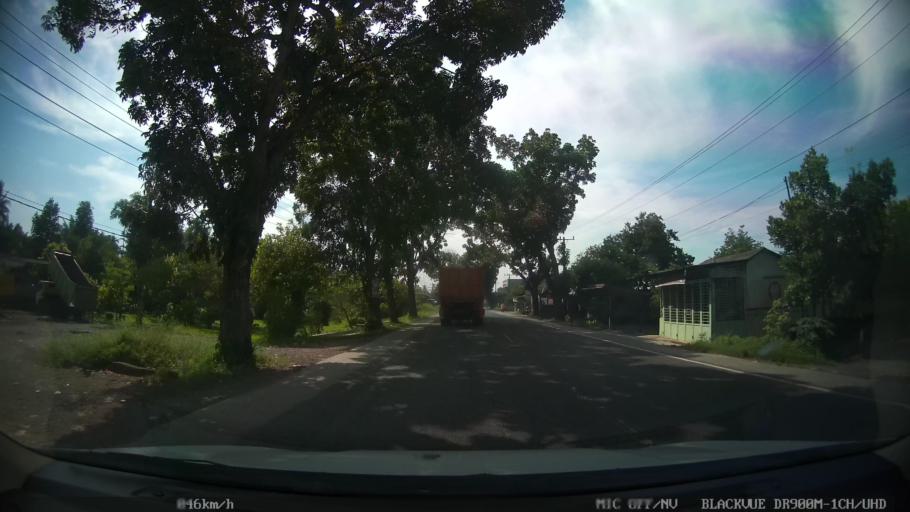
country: ID
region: North Sumatra
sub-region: Kabupaten Langkat
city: Stabat
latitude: 3.7256
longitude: 98.4987
